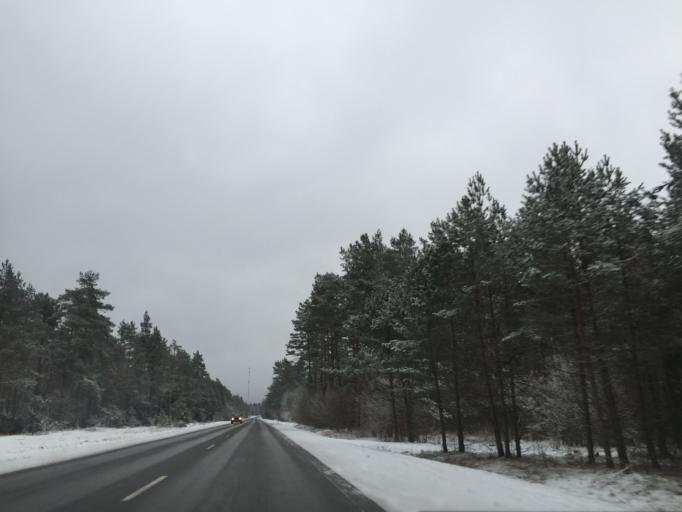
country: EE
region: Laeaene
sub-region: Lihula vald
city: Lihula
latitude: 58.6094
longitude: 23.9428
